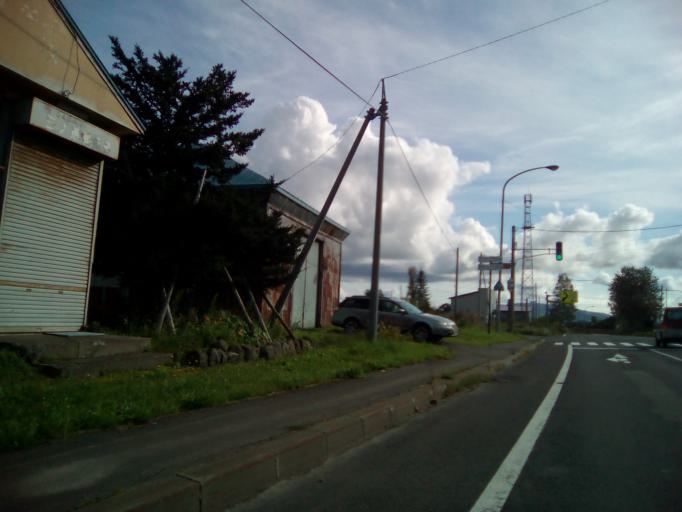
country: JP
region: Hokkaido
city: Niseko Town
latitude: 42.6946
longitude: 140.8396
